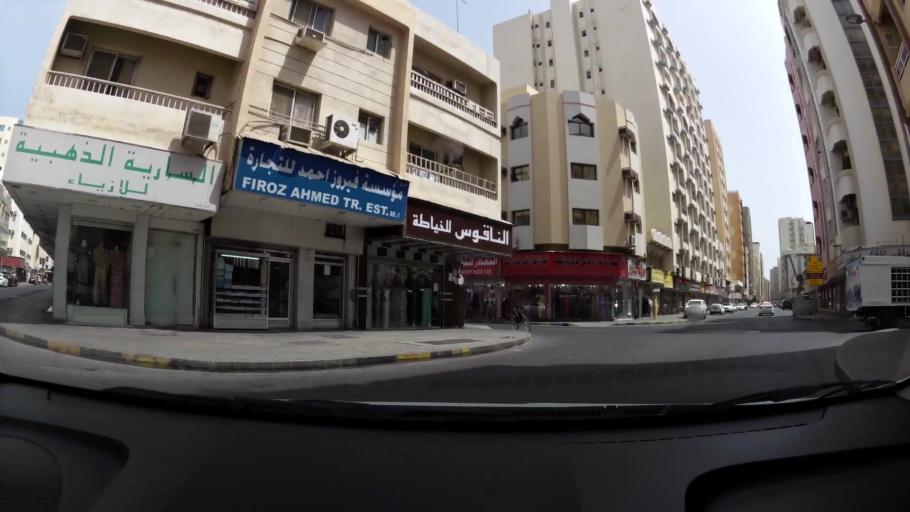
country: AE
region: Ash Shariqah
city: Sharjah
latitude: 25.3595
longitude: 55.3867
